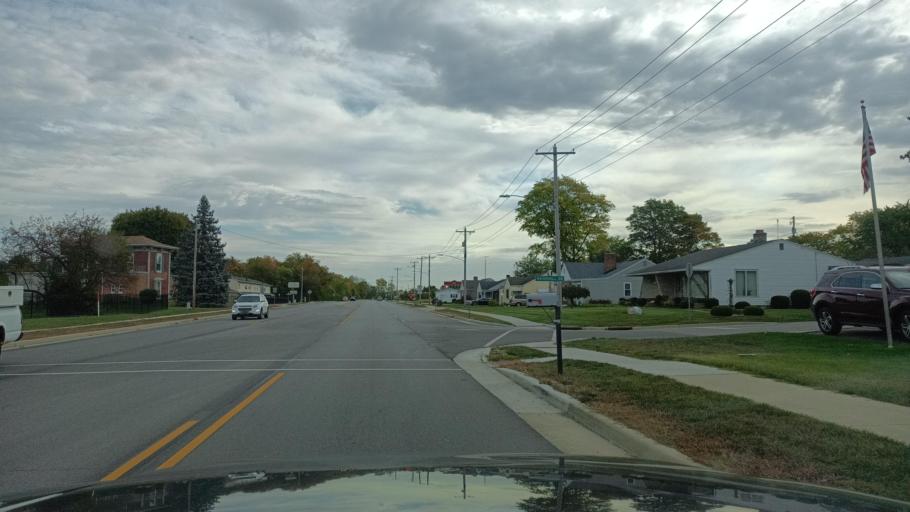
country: US
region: Indiana
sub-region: Delaware County
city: Yorktown
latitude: 40.1799
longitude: -85.4833
